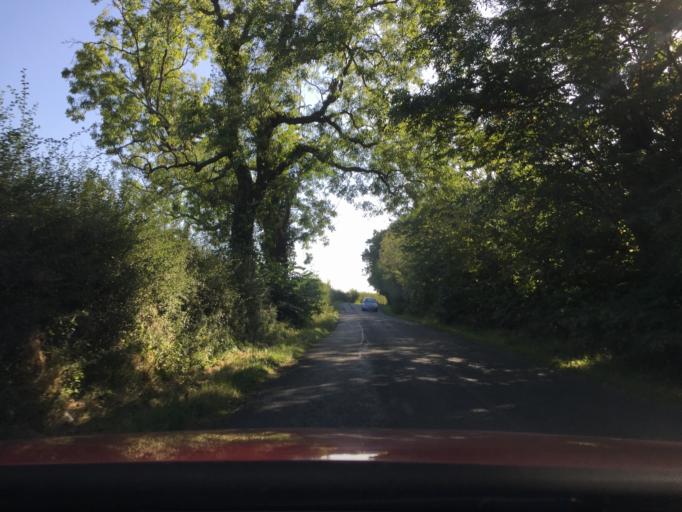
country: GB
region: England
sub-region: Leicestershire
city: Houghton on the Hill
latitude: 52.6440
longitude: -0.9791
